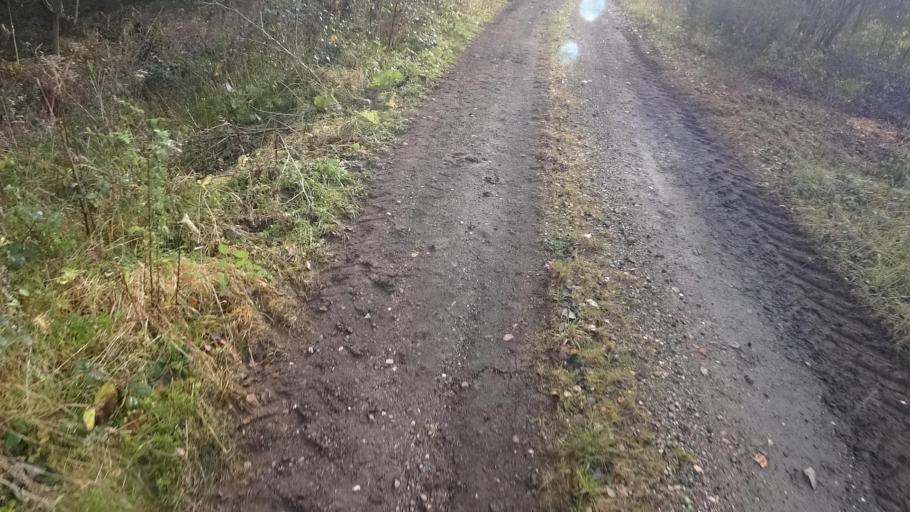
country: DE
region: Rheinland-Pfalz
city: Hausbay
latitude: 50.1042
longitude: 7.5372
